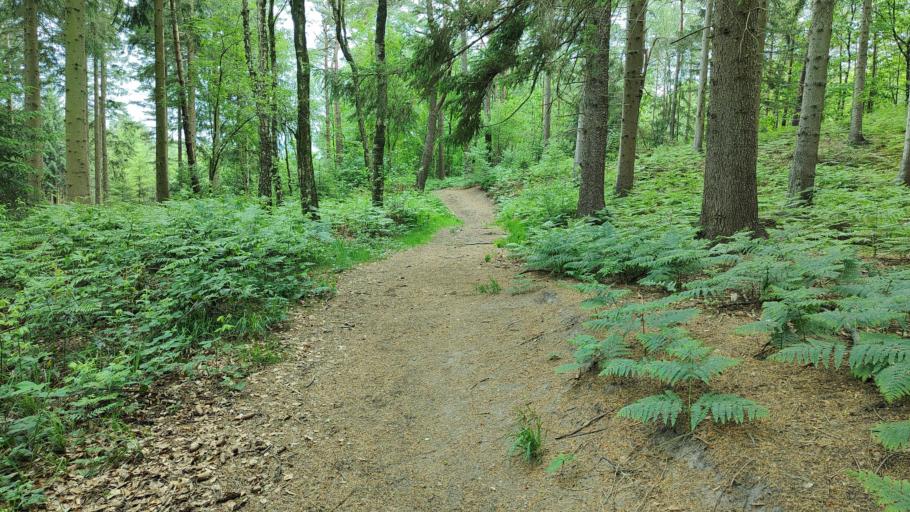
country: BE
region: Wallonia
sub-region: Province de Liege
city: La Calamine
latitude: 50.7142
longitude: 6.0556
